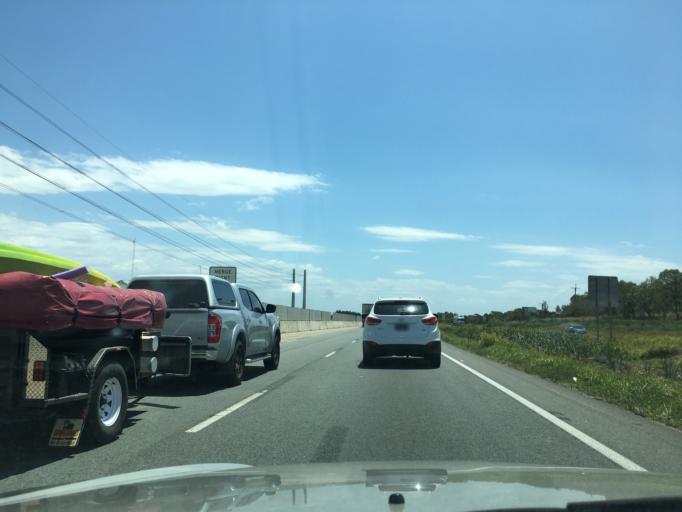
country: AU
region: Queensland
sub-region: Brisbane
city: Shorncliffe
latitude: -27.3603
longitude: 153.0937
